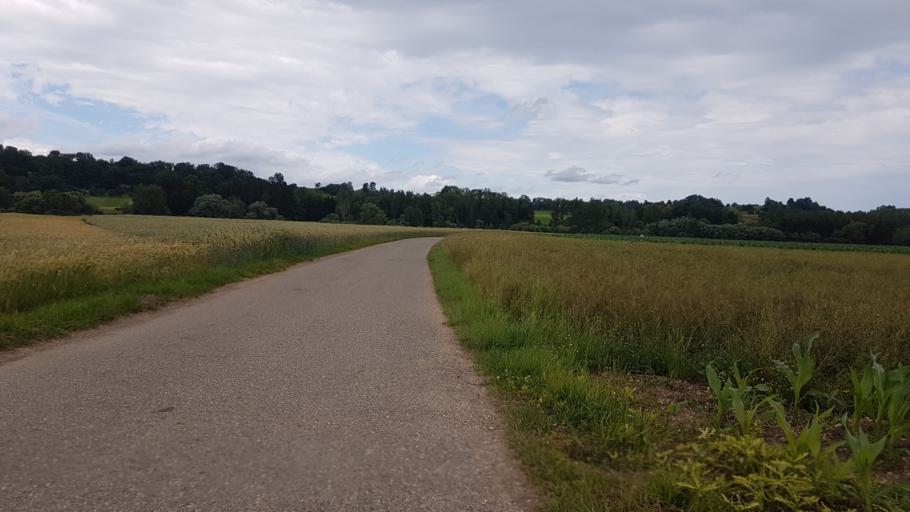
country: DE
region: Baden-Wuerttemberg
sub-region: Tuebingen Region
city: Hohentengen
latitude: 48.0674
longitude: 9.3668
